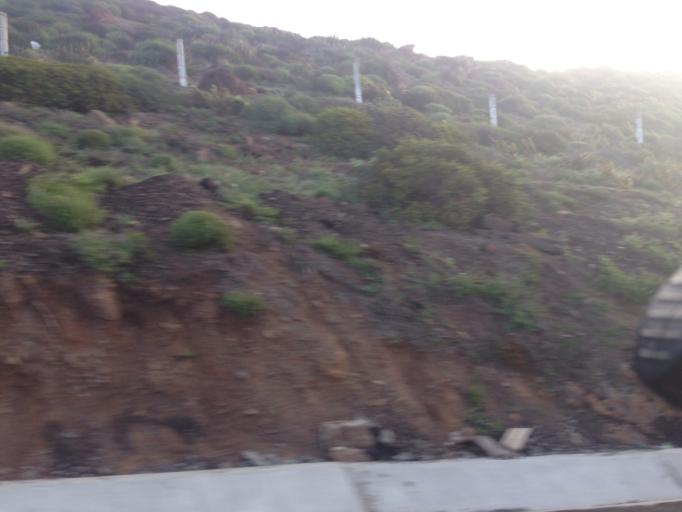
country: MX
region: Baja California
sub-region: Playas de Rosarito
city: Santa Anita
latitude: 32.1301
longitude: -116.8848
